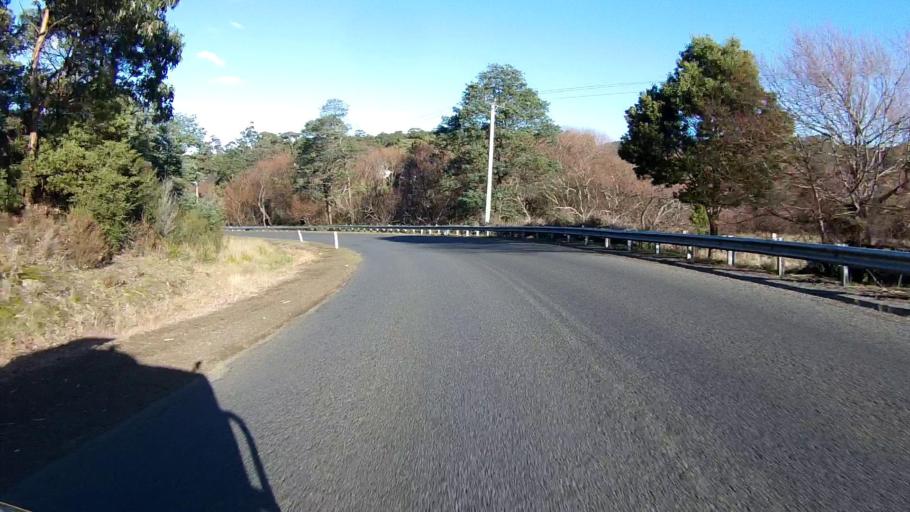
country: AU
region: Tasmania
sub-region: Clarence
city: Sandford
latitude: -43.1497
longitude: 147.8435
